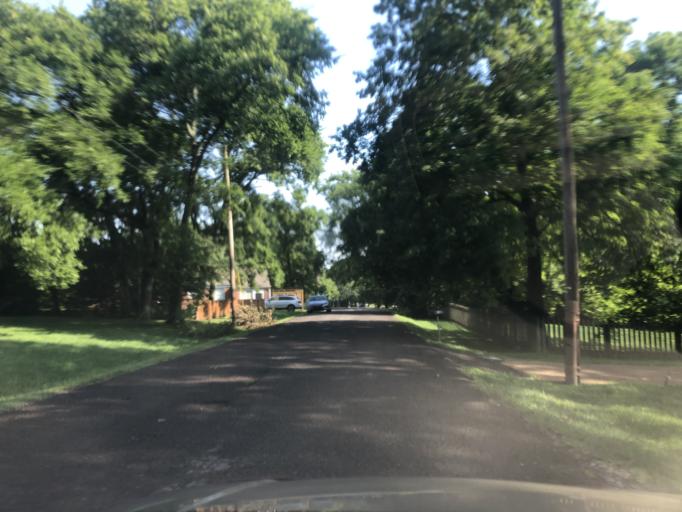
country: US
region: Tennessee
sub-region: Davidson County
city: Lakewood
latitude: 36.2307
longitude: -86.7162
